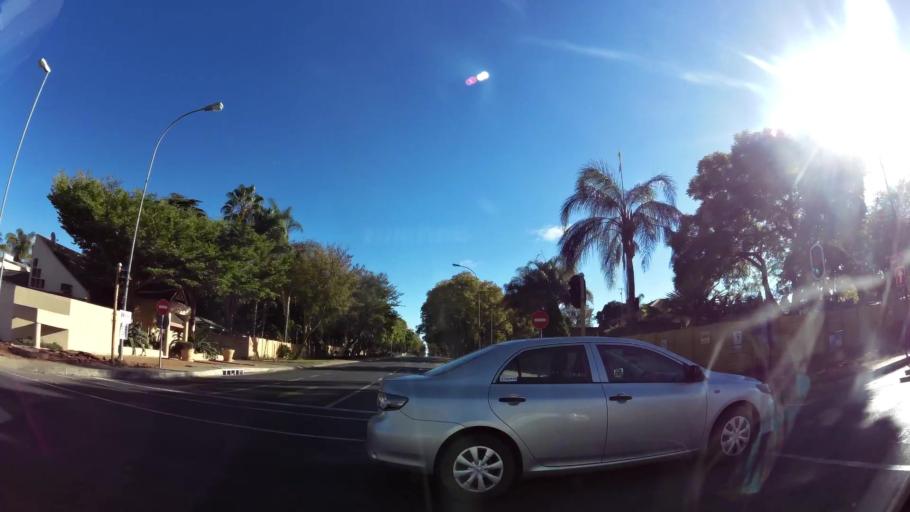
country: ZA
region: Limpopo
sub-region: Capricorn District Municipality
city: Polokwane
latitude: -23.9166
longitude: 29.4617
